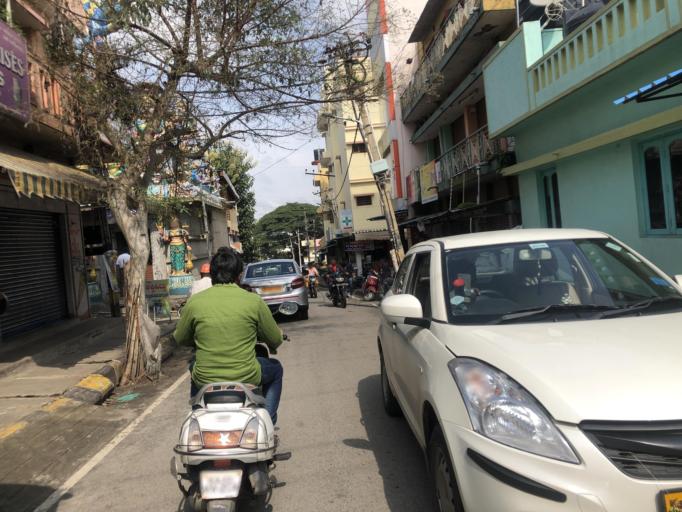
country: IN
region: Karnataka
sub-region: Bangalore Urban
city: Bangalore
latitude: 12.9295
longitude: 77.5366
